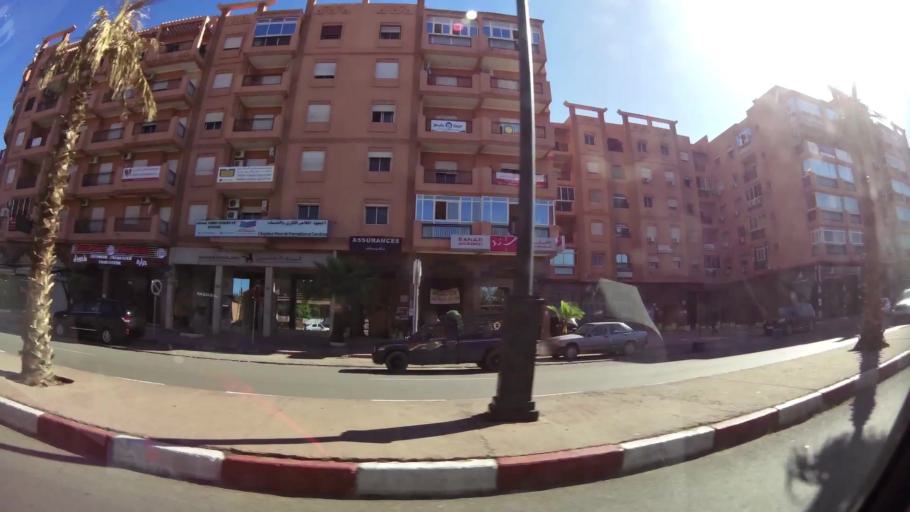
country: MA
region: Marrakech-Tensift-Al Haouz
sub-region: Marrakech
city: Marrakesh
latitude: 31.6371
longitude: -8.0020
